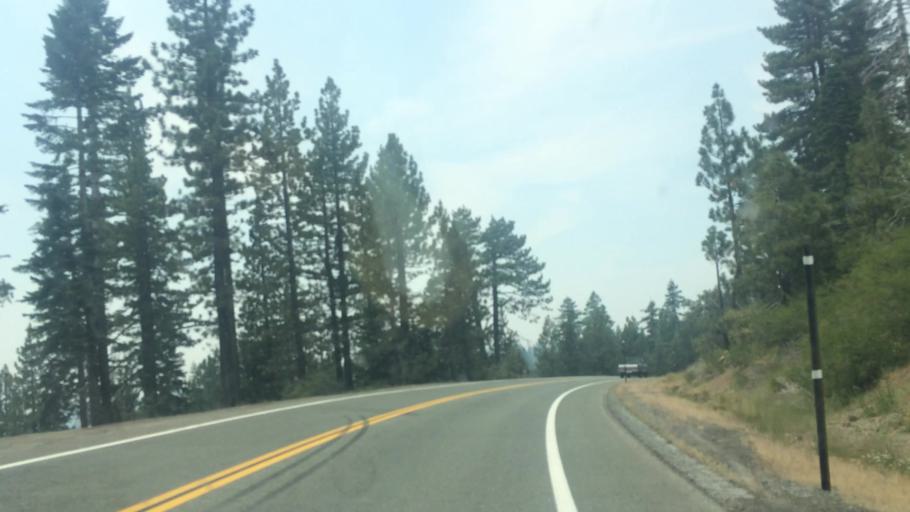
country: US
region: California
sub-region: Calaveras County
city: Arnold
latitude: 38.5857
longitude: -120.2382
